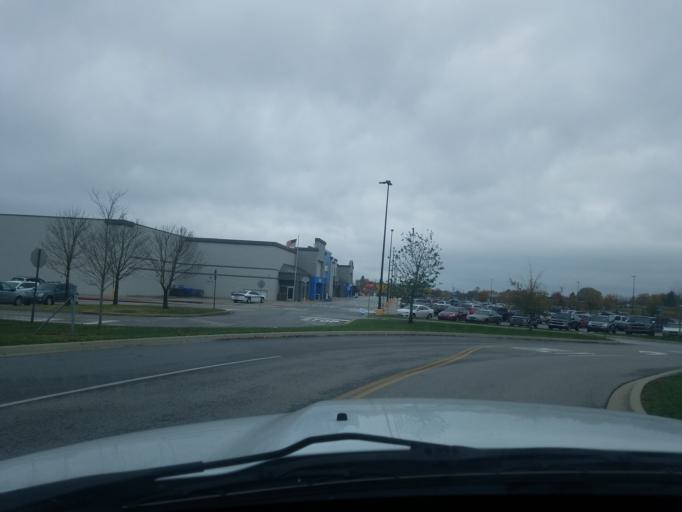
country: US
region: Kentucky
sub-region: Marion County
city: Lebanon
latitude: 37.5537
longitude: -85.2823
